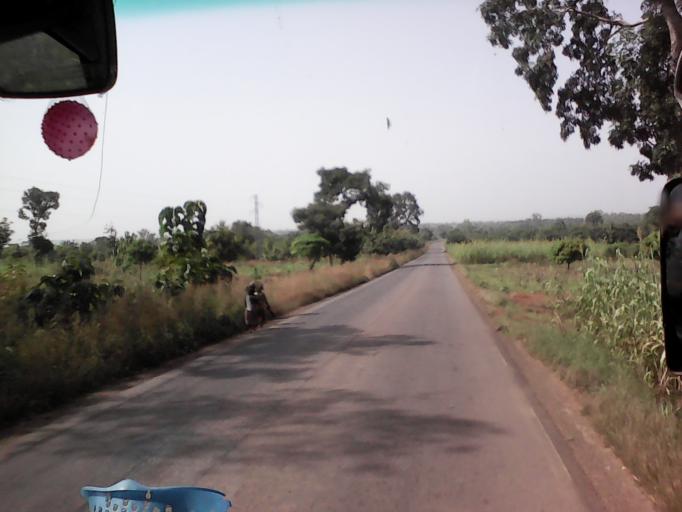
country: TG
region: Centrale
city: Sokode
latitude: 8.9131
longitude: 1.1022
